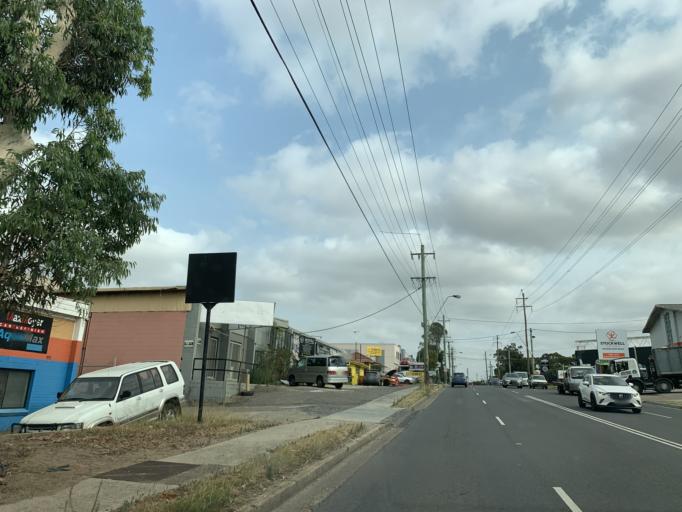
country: AU
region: New South Wales
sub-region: Blacktown
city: Blacktown
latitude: -33.7712
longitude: 150.9437
